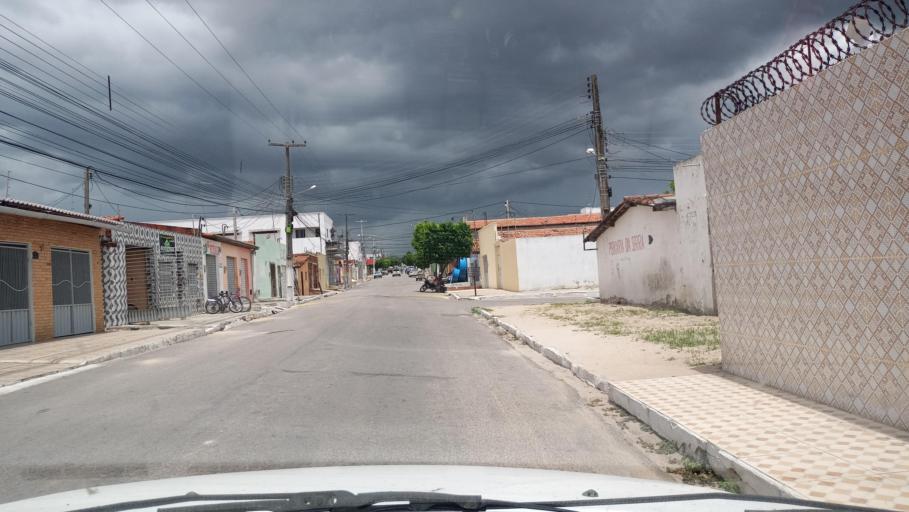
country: BR
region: Rio Grande do Norte
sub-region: Tangara
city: Tangara
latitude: -6.1021
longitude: -35.7118
